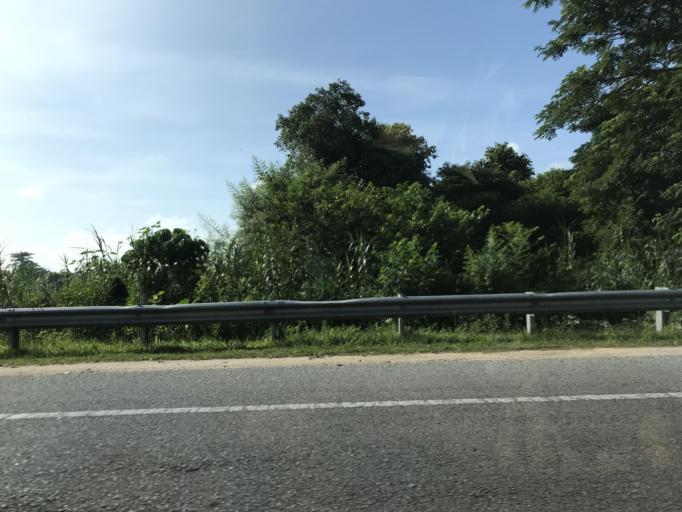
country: MY
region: Kelantan
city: Kampong Kadok
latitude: 6.0549
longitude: 102.2269
